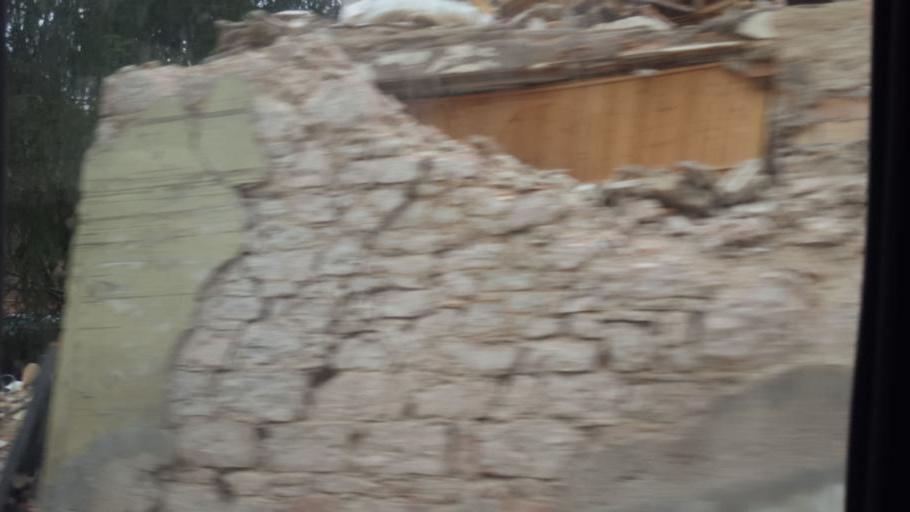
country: IT
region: The Marches
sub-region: Provincia di Macerata
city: Visso
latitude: 42.9459
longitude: 13.0833
